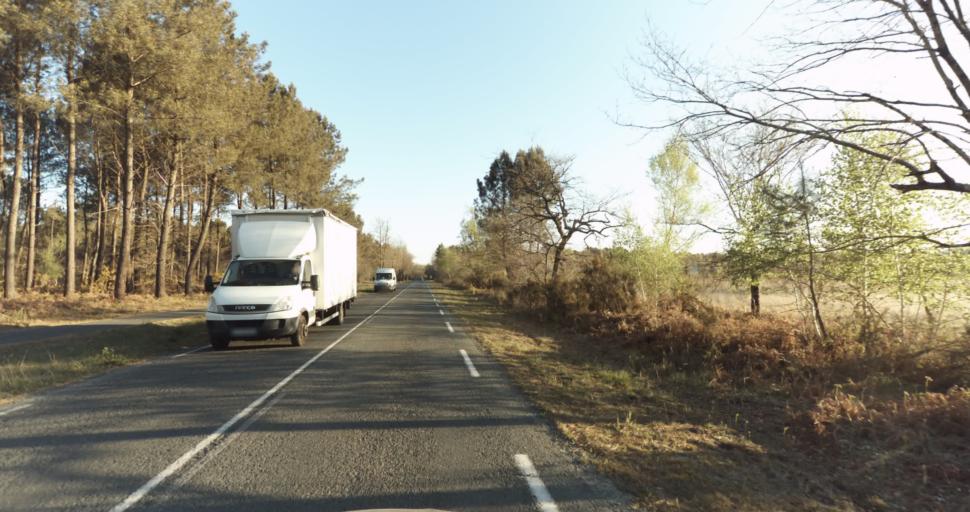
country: FR
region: Aquitaine
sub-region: Departement de la Gironde
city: Martignas-sur-Jalle
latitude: 44.8231
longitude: -0.7784
